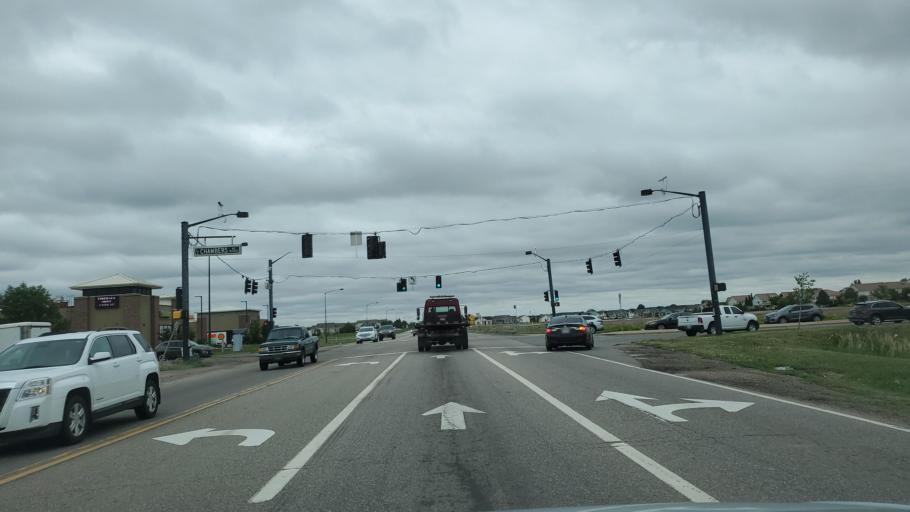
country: US
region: Colorado
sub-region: Adams County
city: Brighton
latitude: 39.9144
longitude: -104.8098
